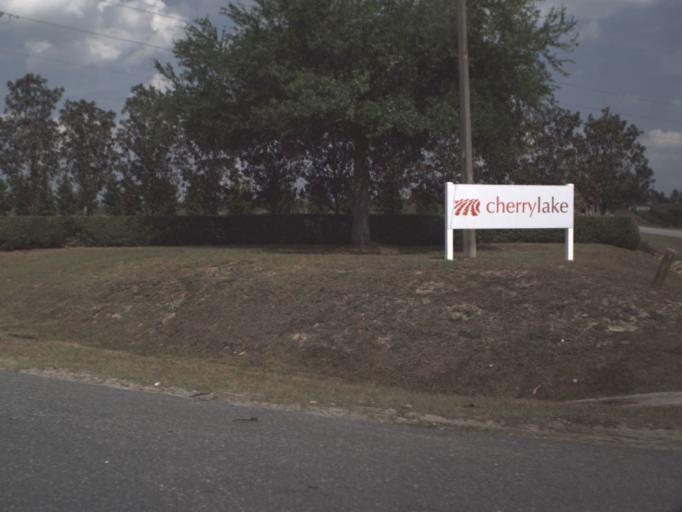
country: US
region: Florida
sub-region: Lake County
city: Groveland
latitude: 28.5875
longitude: -81.8517
